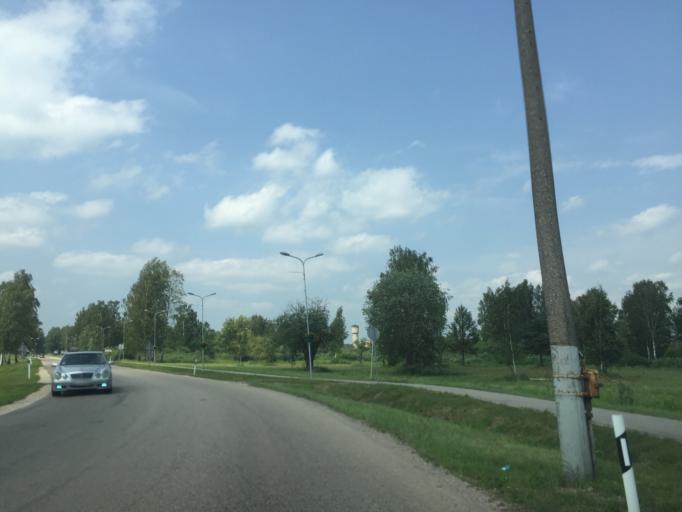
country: LV
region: Olaine
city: Olaine
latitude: 56.7906
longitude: 23.9541
